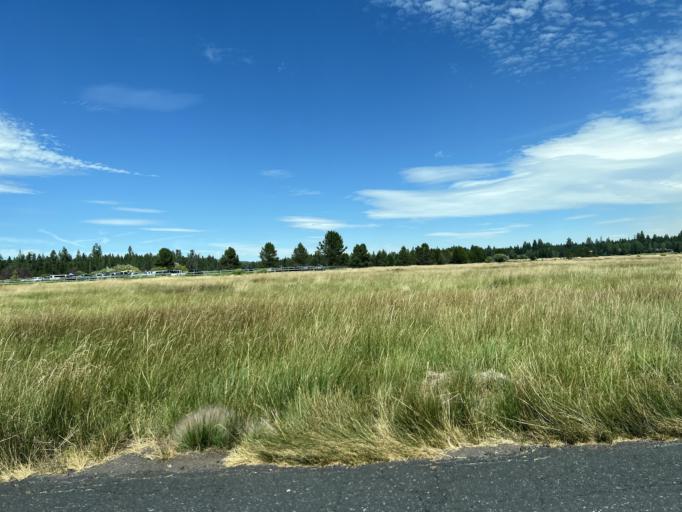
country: US
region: Oregon
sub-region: Deschutes County
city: Sunriver
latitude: 43.8851
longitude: -121.4547
